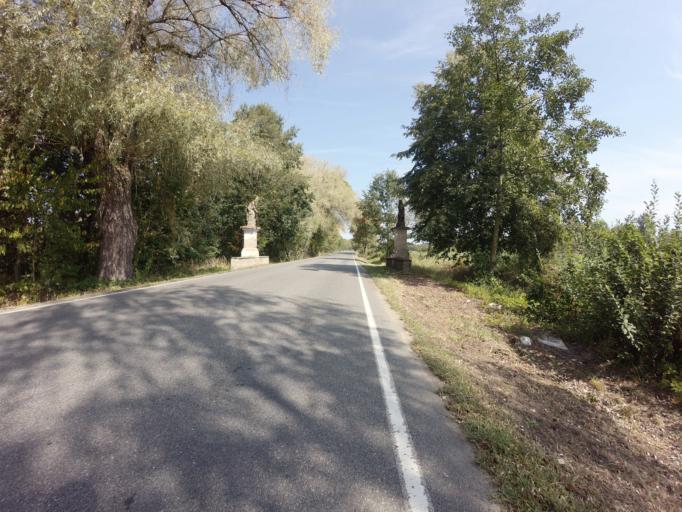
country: CZ
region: Central Bohemia
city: Sedlcany
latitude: 49.6069
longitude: 14.3844
